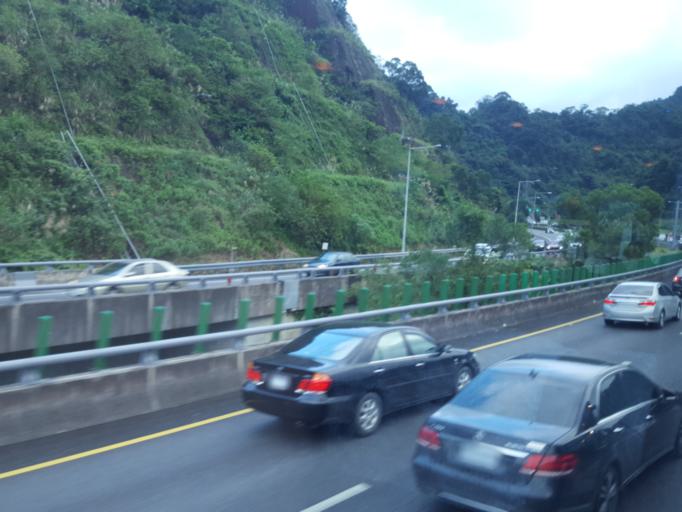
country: TW
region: Taipei
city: Taipei
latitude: 24.9831
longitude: 121.6617
